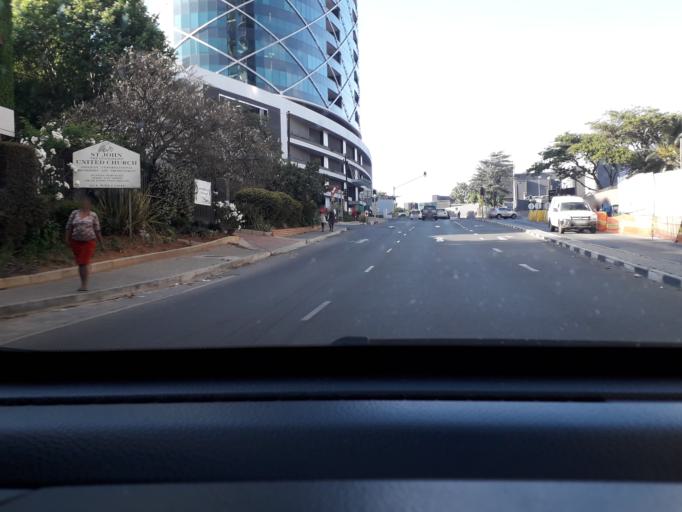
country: ZA
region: Gauteng
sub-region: City of Johannesburg Metropolitan Municipality
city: Johannesburg
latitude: -26.0981
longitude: 28.0508
